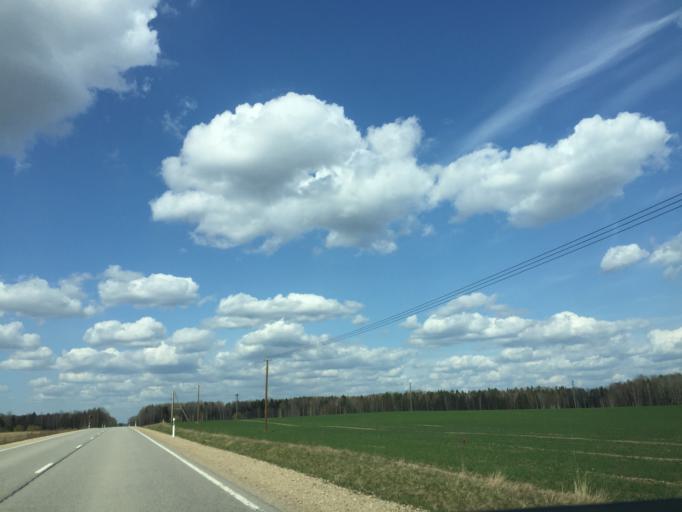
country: LV
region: Skriveri
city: Skriveri
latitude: 56.7691
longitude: 25.1678
